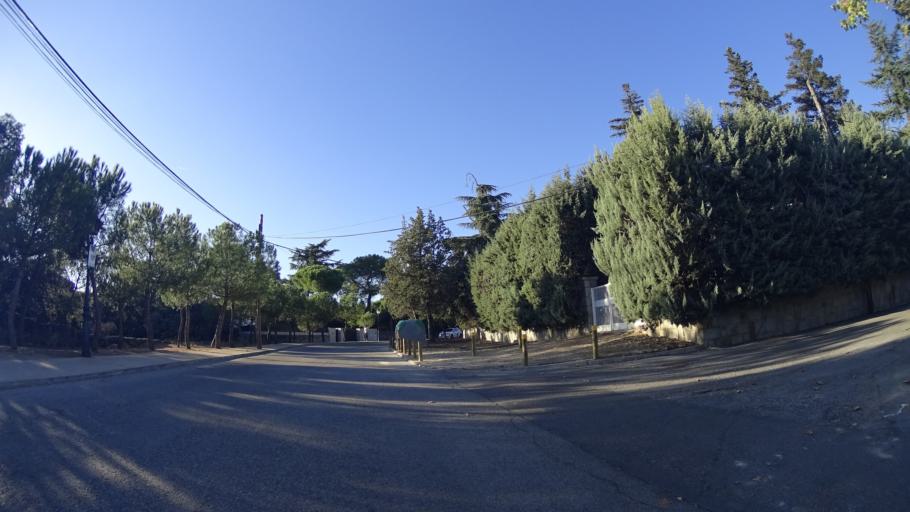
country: ES
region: Madrid
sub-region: Provincia de Madrid
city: Torrelodones
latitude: 40.5739
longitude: -3.9484
